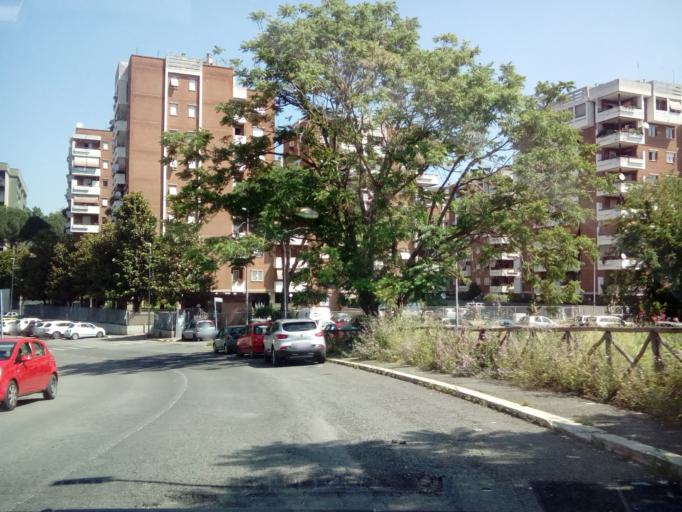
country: IT
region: Latium
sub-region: Citta metropolitana di Roma Capitale
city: Rome
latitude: 41.8821
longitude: 12.5913
